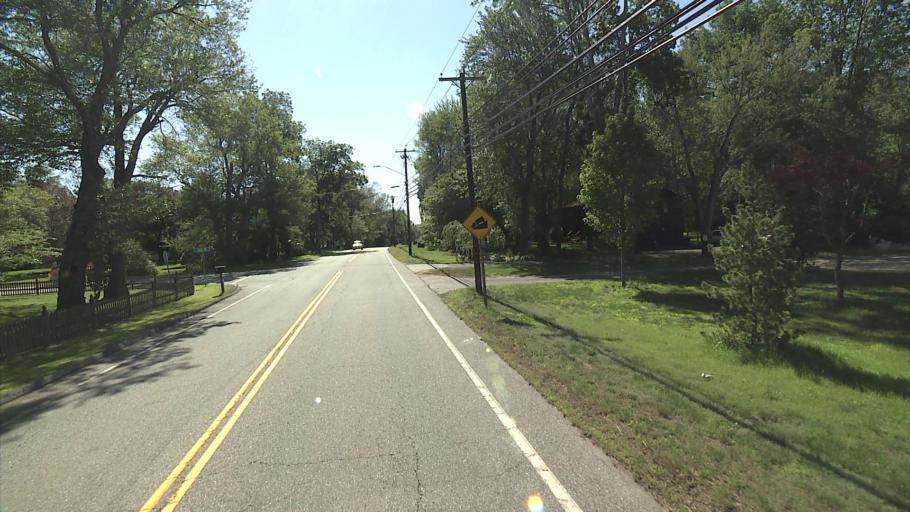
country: US
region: Connecticut
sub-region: Middlesex County
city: East Hampton
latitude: 41.5666
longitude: -72.4841
